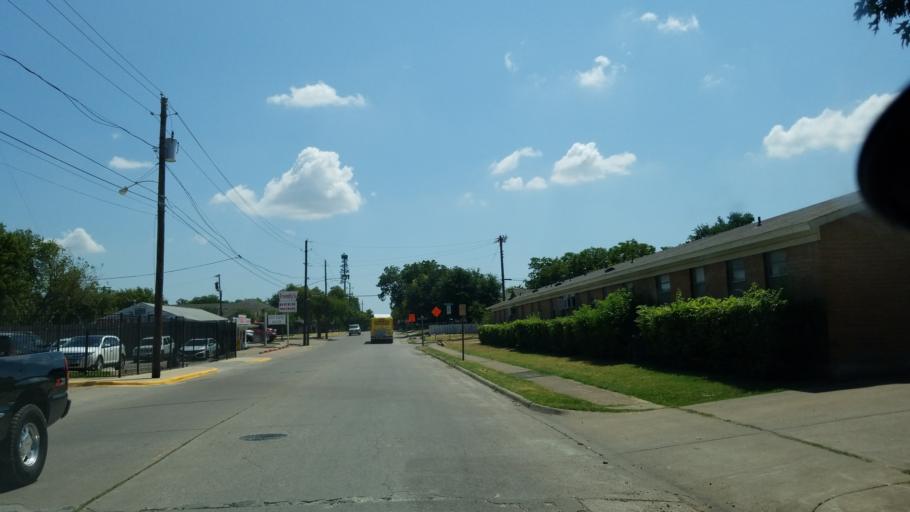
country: US
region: Texas
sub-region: Dallas County
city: Cockrell Hill
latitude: 32.7350
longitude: -96.8885
